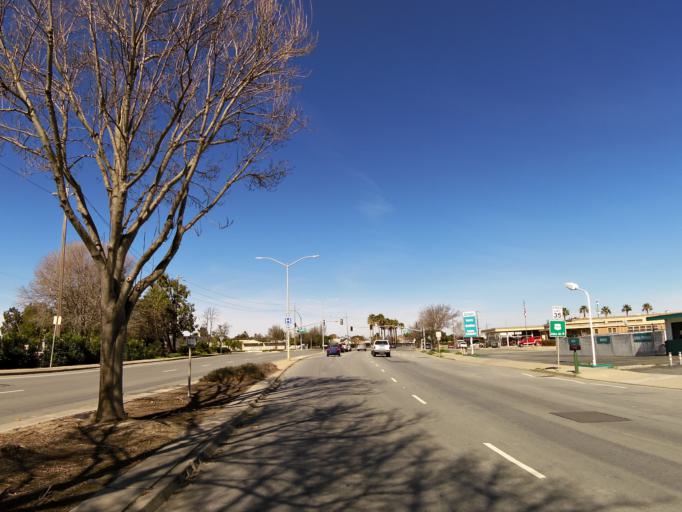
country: US
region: California
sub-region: Monterey County
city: Salinas
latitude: 36.6585
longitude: -121.6376
